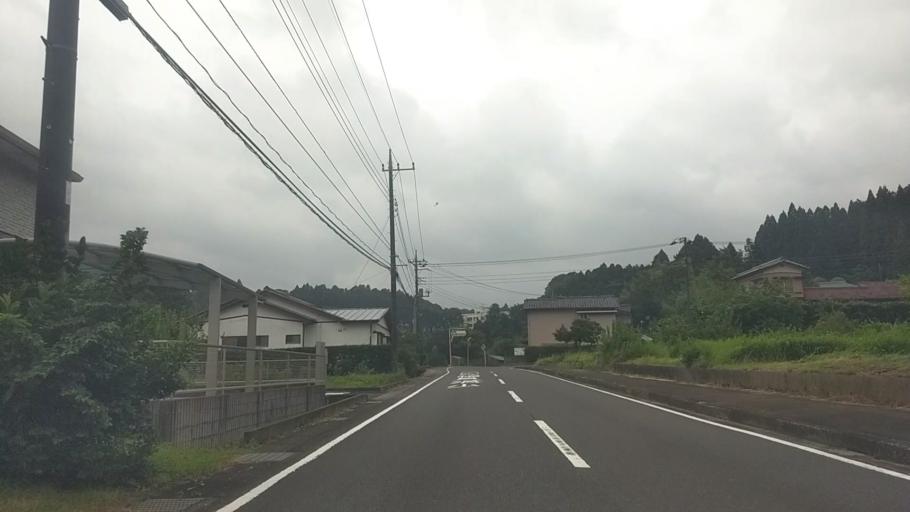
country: JP
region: Chiba
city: Kawaguchi
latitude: 35.2563
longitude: 140.0573
